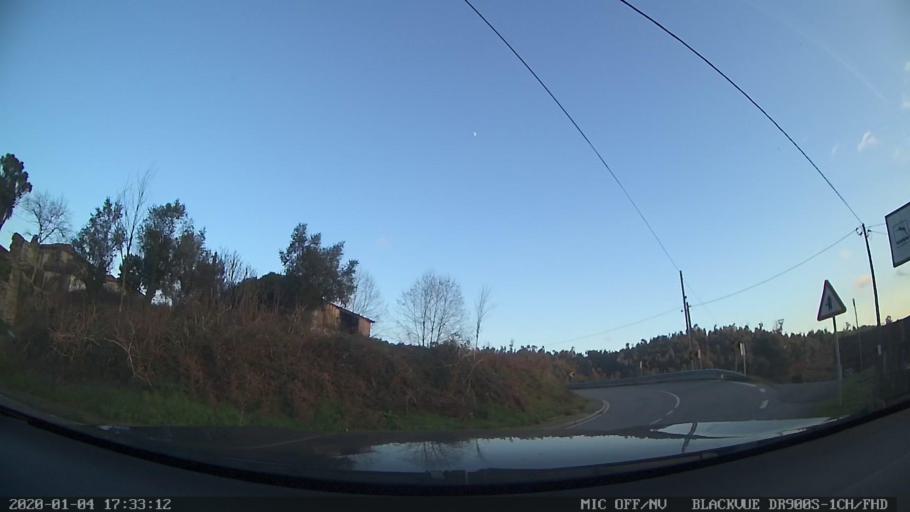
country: PT
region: Vila Real
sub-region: Mondim de Basto
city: Mondim de Basto
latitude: 41.4333
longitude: -7.9799
